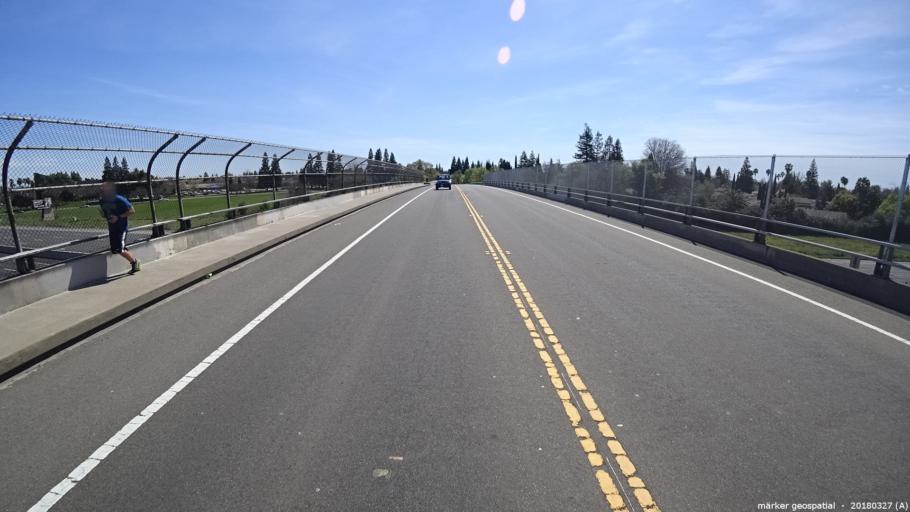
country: US
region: California
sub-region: Sacramento County
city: La Riviera
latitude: 38.5624
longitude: -121.3494
